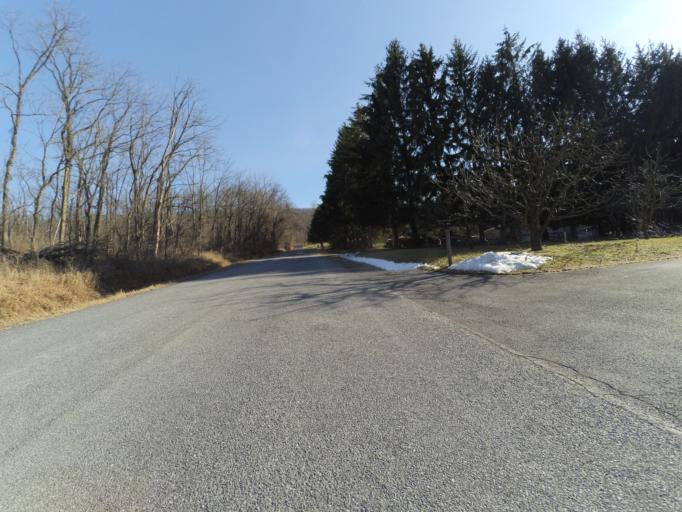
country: US
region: Pennsylvania
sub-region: Centre County
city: Lemont
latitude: 40.8214
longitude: -77.8026
